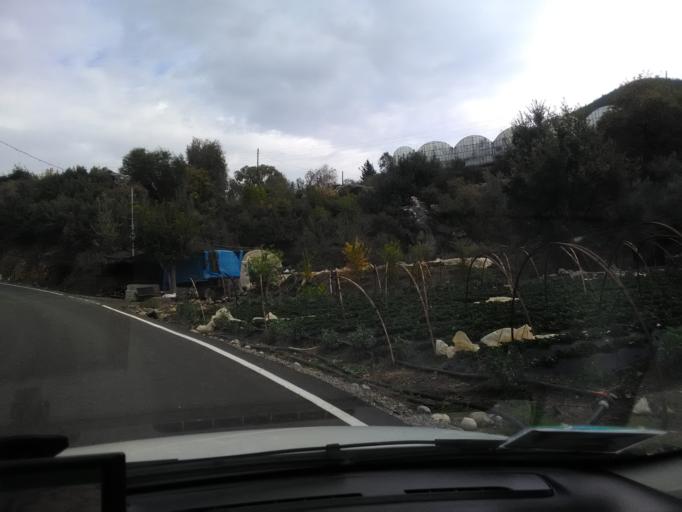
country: TR
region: Antalya
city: Gazipasa
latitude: 36.2593
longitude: 32.3642
